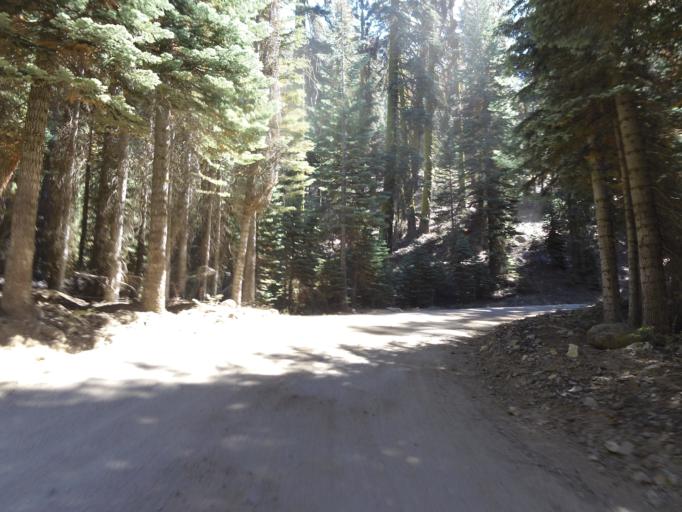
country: US
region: California
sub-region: Madera County
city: Oakhurst
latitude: 37.4303
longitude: -119.5007
